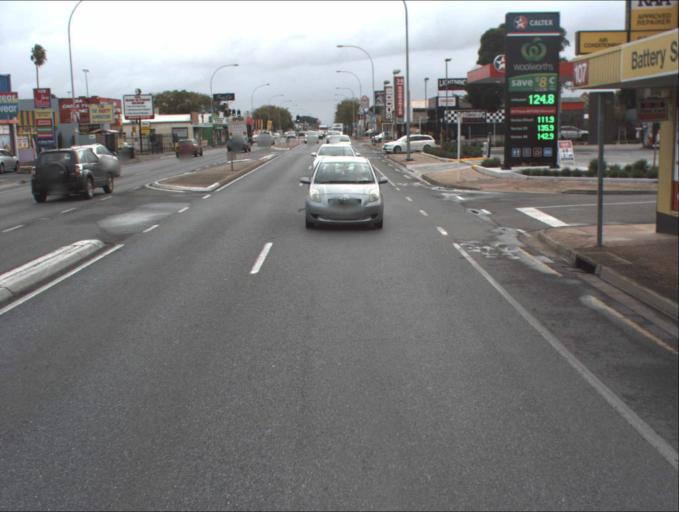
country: AU
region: South Australia
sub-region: Prospect
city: Prospect
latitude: -34.8882
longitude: 138.6031
